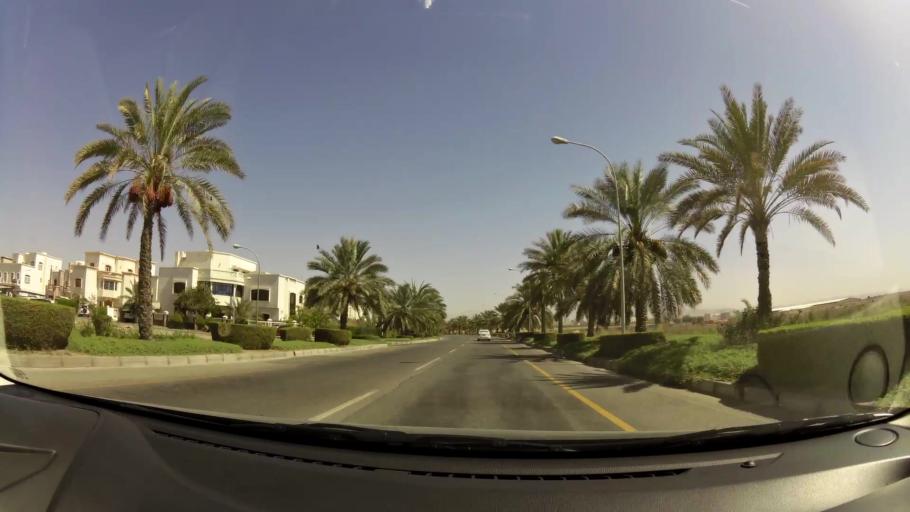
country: OM
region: Muhafazat Masqat
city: Bawshar
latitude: 23.5993
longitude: 58.3471
